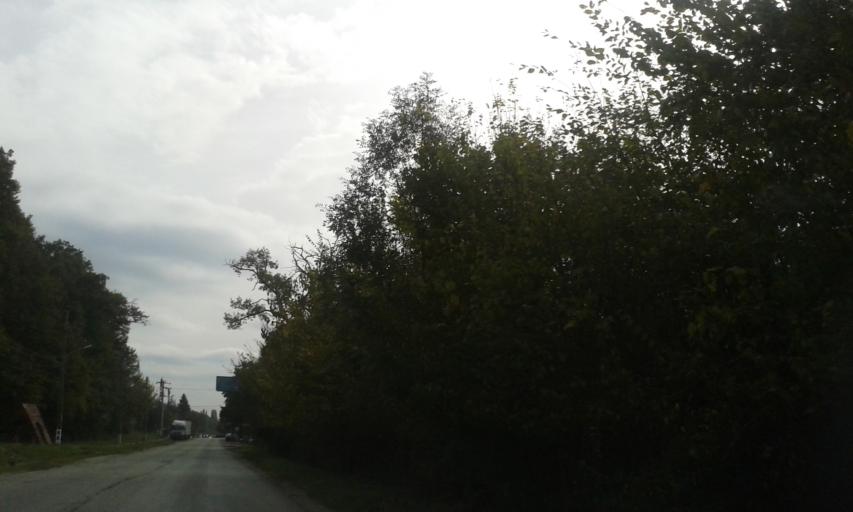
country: RO
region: Gorj
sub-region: Comuna Targu Carbunesti
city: Targu Carbunesti
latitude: 44.9660
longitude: 23.5050
